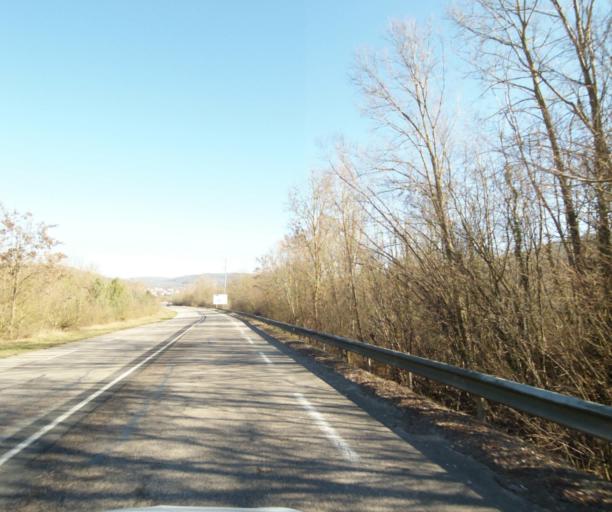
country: FR
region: Lorraine
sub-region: Departement de Meurthe-et-Moselle
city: Lay-Saint-Christophe
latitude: 48.7376
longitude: 6.1838
